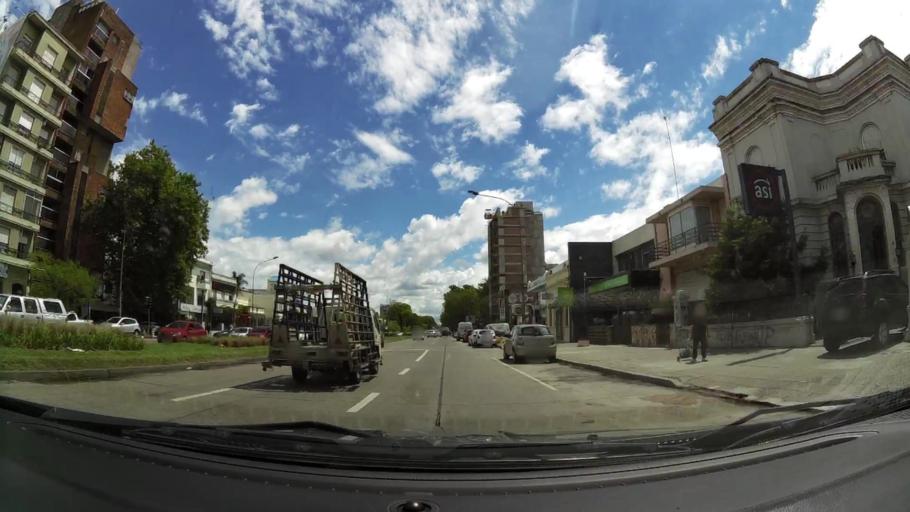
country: UY
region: Montevideo
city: Montevideo
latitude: -34.8909
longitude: -56.1653
